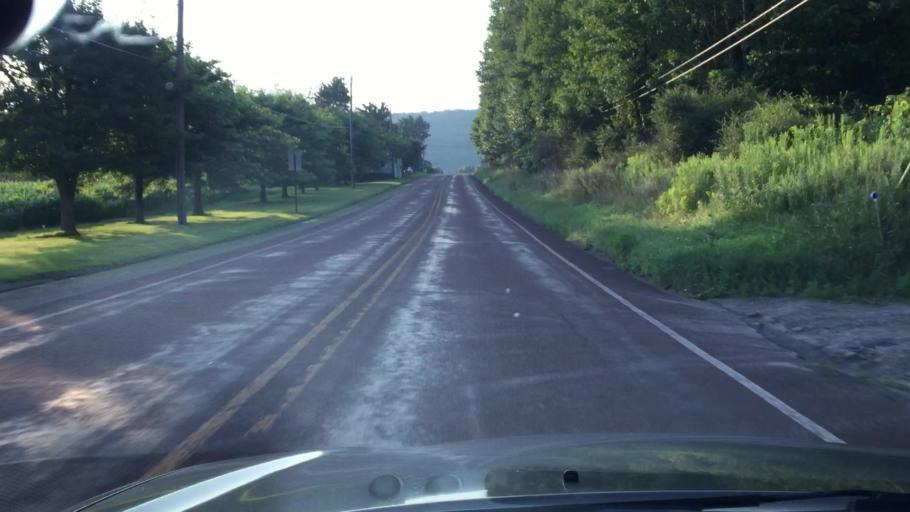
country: US
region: Pennsylvania
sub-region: Carbon County
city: Weatherly
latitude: 40.9222
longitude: -75.8626
